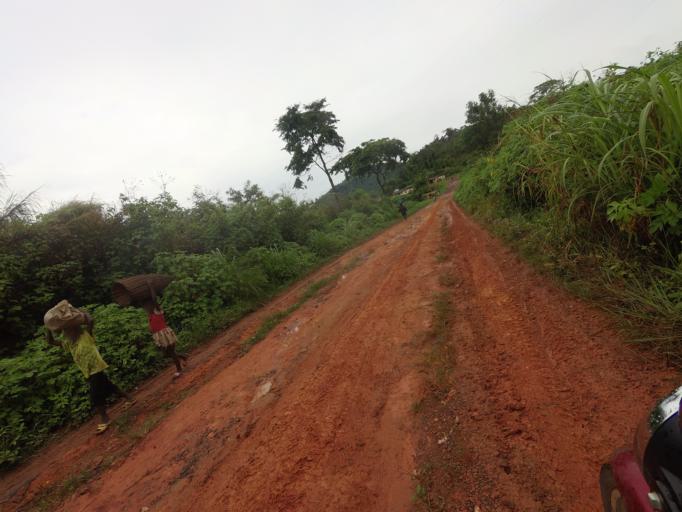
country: LR
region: Nimba
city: New Yekepa
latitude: 7.5662
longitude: -8.5517
